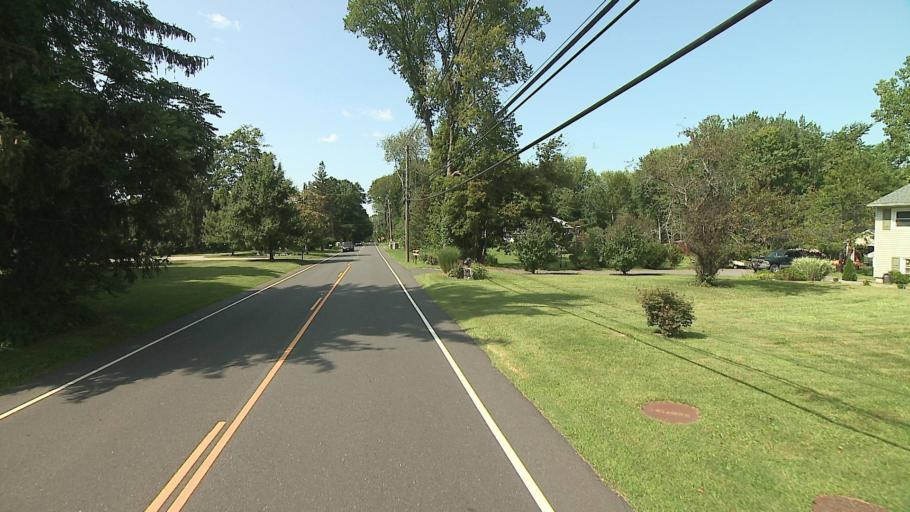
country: US
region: Connecticut
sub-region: Fairfield County
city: Newtown
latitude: 41.4521
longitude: -73.3788
